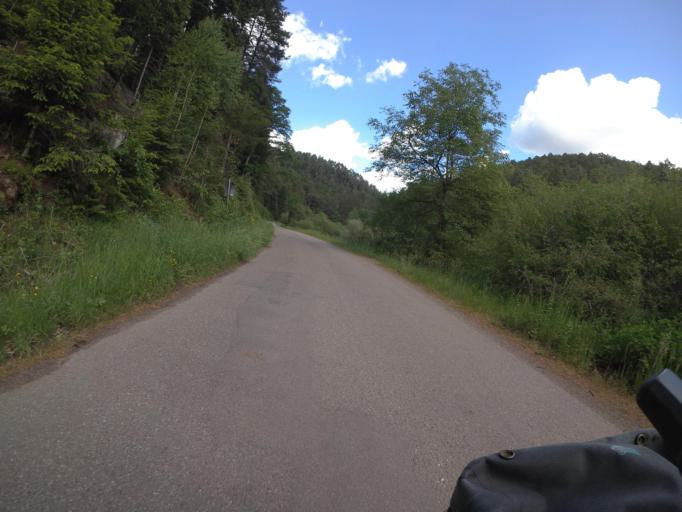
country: DE
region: Rheinland-Pfalz
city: Dahn
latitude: 49.1549
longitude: 7.7589
